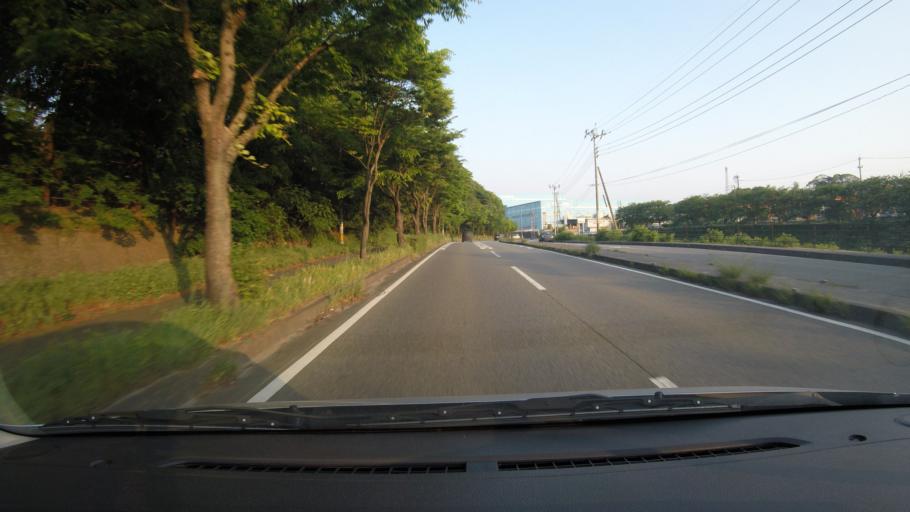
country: JP
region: Fukuoka
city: Sasaguri
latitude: 33.6507
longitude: 130.4927
